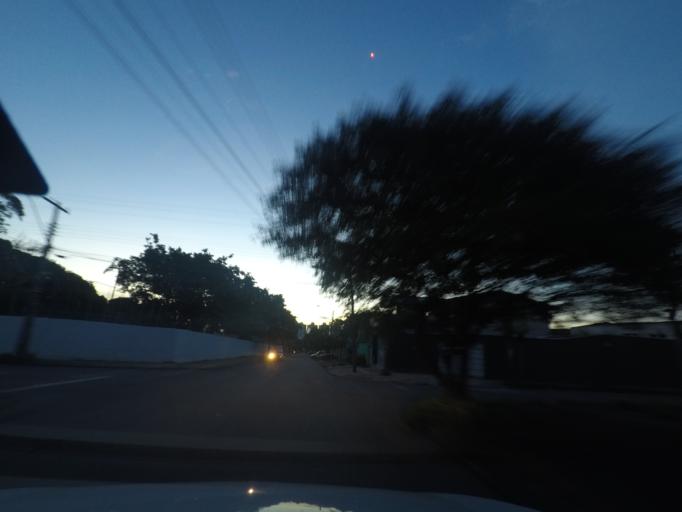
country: BR
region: Goias
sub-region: Goiania
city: Goiania
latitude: -16.7129
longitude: -49.3120
